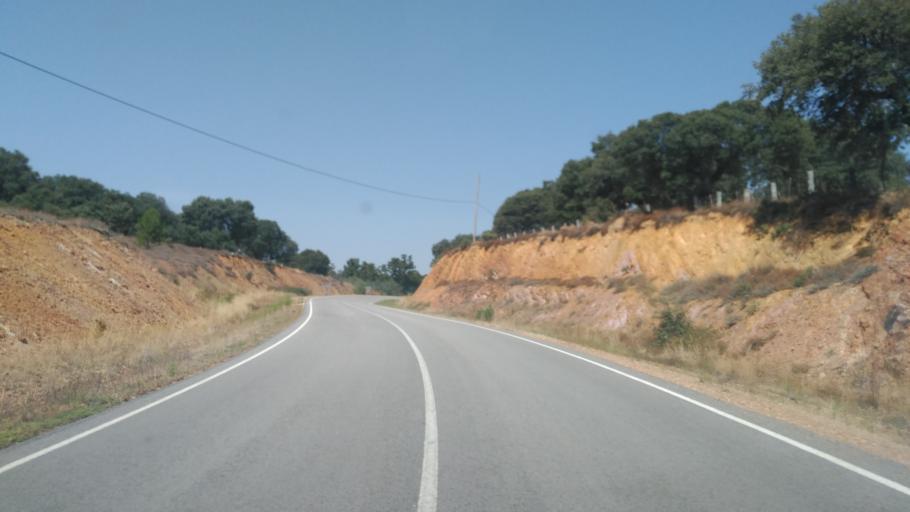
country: ES
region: Castille and Leon
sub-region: Provincia de Salamanca
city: Aldeanueva de la Sierra
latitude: 40.6160
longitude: -6.1393
